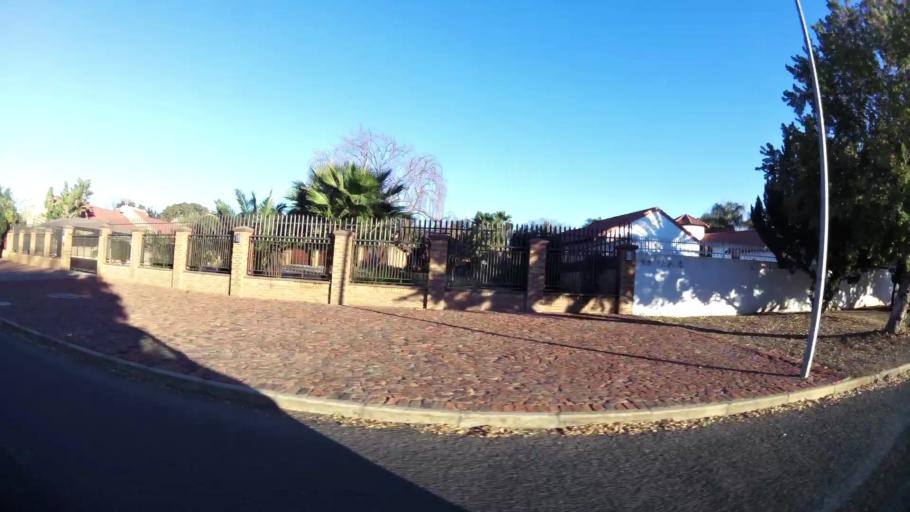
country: ZA
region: Northern Cape
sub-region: Frances Baard District Municipality
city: Kimberley
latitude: -28.7604
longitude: 24.7656
